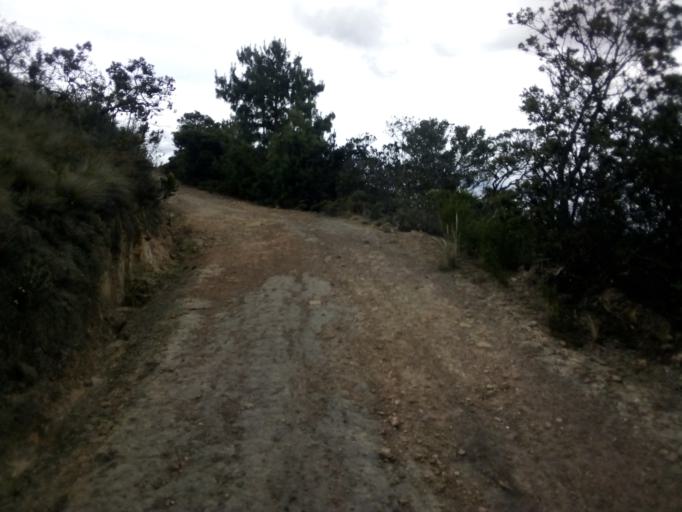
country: CO
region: Boyaca
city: Toca
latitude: 5.5965
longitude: -73.1213
